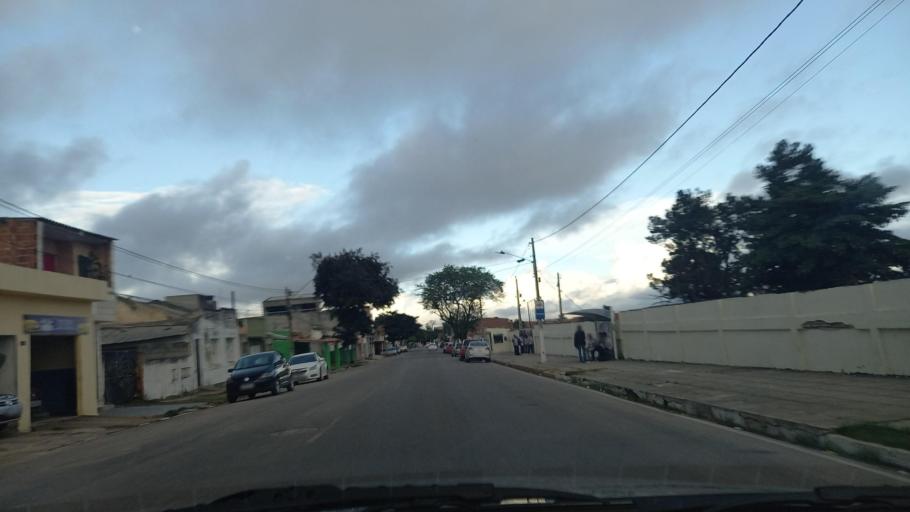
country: BR
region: Pernambuco
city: Garanhuns
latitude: -8.8854
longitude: -36.5056
